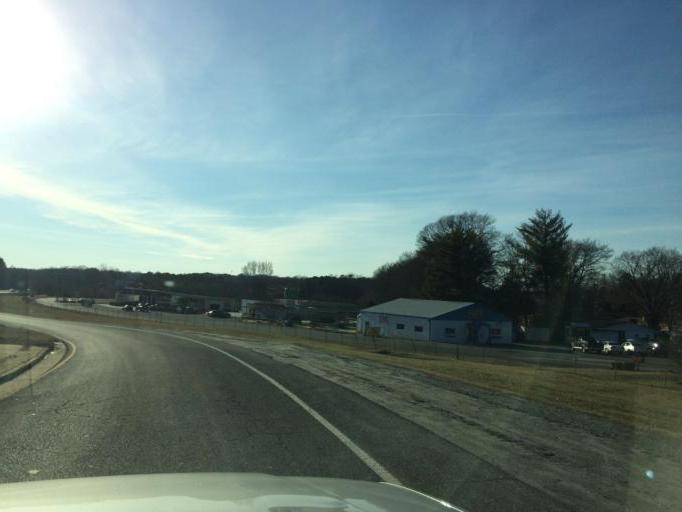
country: US
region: North Carolina
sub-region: Rutherford County
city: Forest City
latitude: 35.3166
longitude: -81.8579
